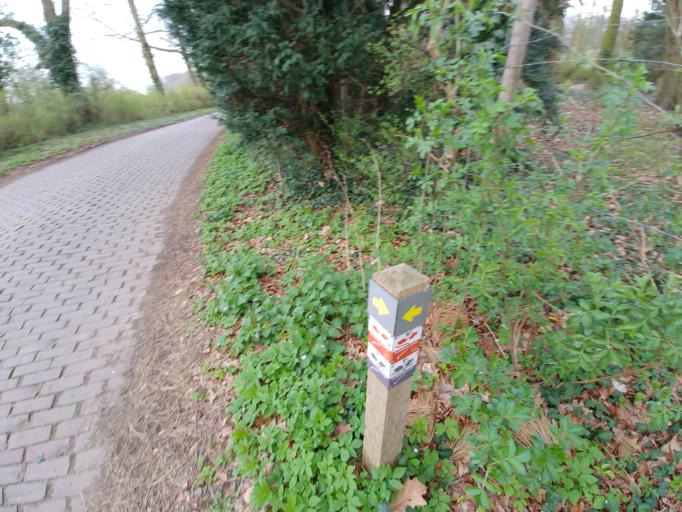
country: NL
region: Gelderland
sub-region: Gemeente Voorst
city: Twello
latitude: 52.2509
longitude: 6.1187
